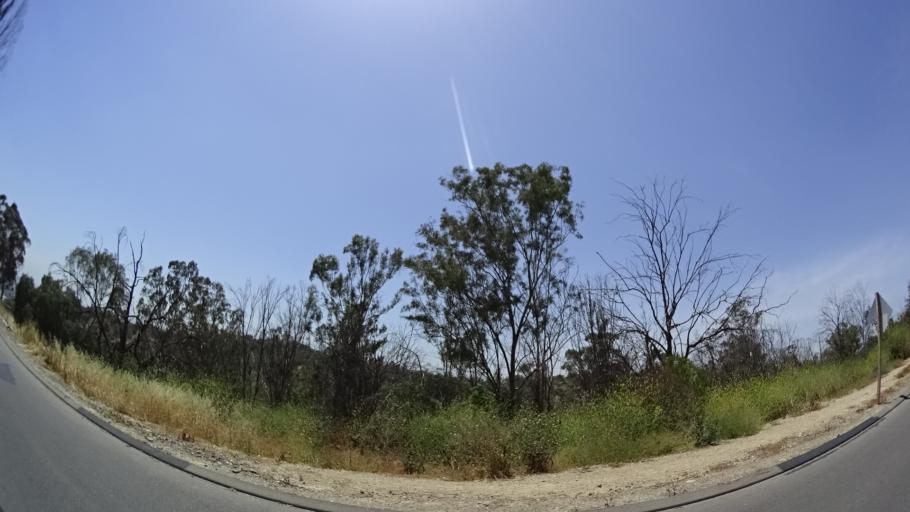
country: US
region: California
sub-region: Los Angeles County
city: Echo Park
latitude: 34.0786
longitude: -118.2326
